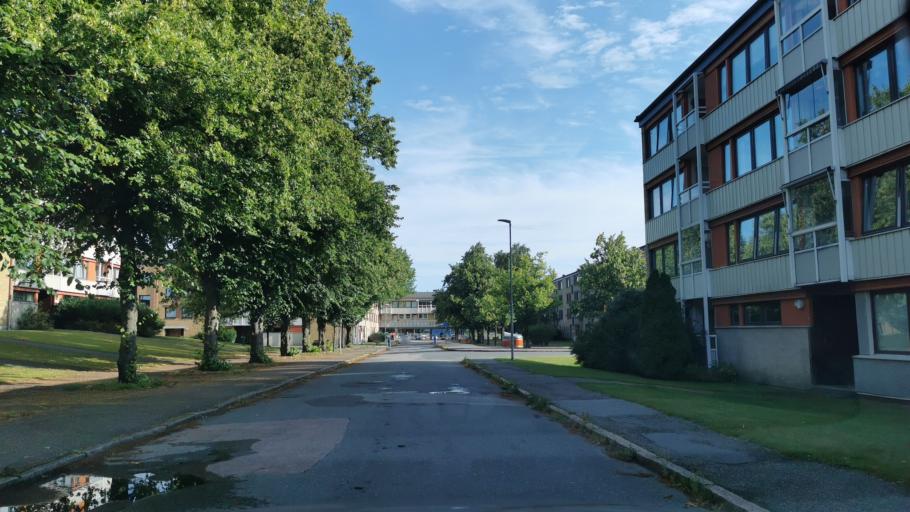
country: SE
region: Vaestra Goetaland
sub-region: Goteborg
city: Majorna
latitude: 57.6610
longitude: 11.9281
